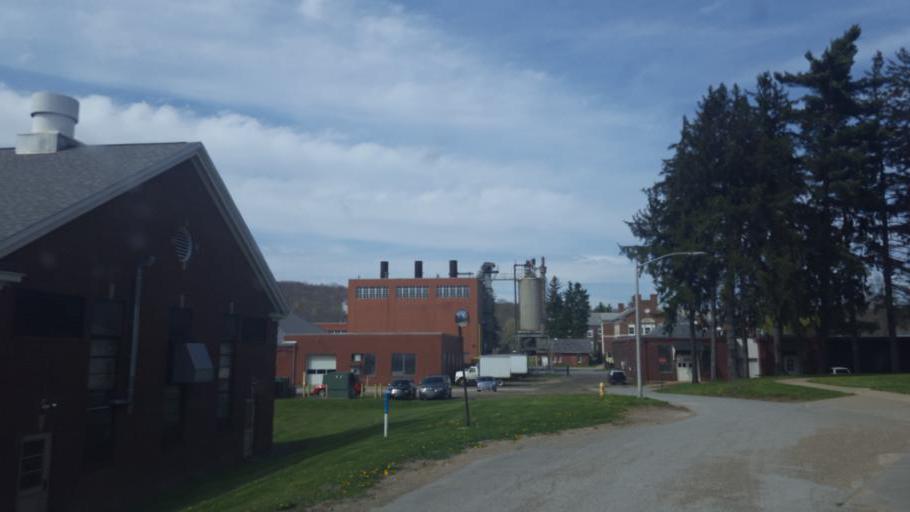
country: US
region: Pennsylvania
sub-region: Venango County
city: Sugarcreek
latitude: 41.3705
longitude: -79.9330
